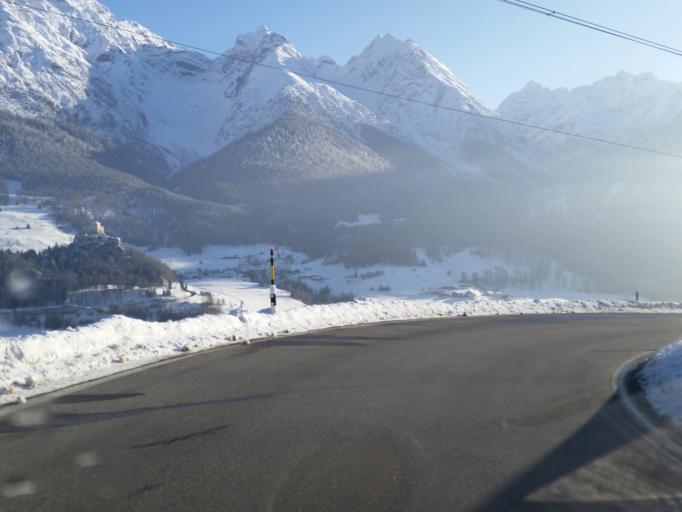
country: CH
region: Grisons
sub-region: Inn District
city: Scuol
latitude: 46.7910
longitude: 10.2559
